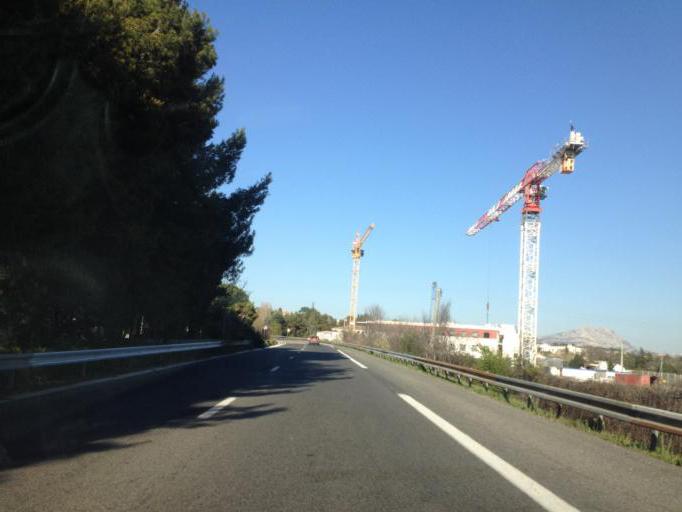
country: FR
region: Provence-Alpes-Cote d'Azur
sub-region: Departement des Bouches-du-Rhone
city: Aix-en-Provence
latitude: 43.5129
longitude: 5.4260
